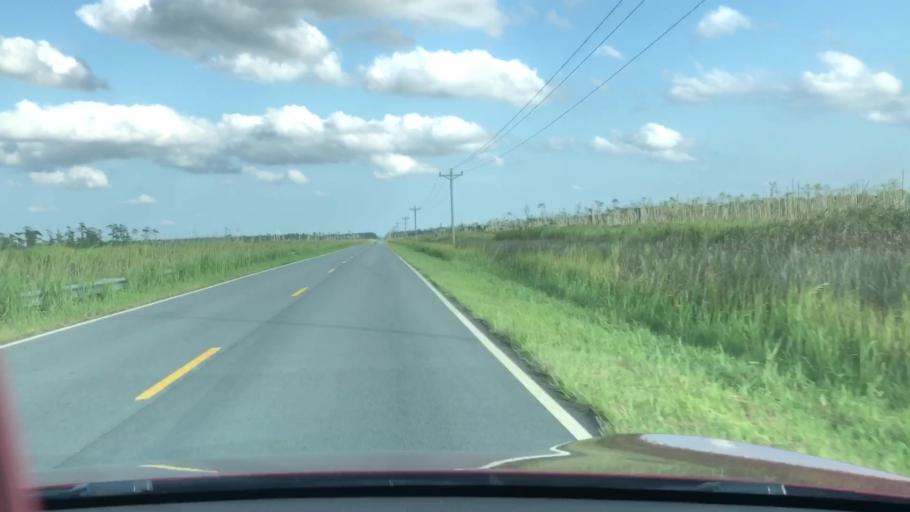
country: US
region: North Carolina
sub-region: Dare County
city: Wanchese
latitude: 35.6304
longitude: -75.8532
